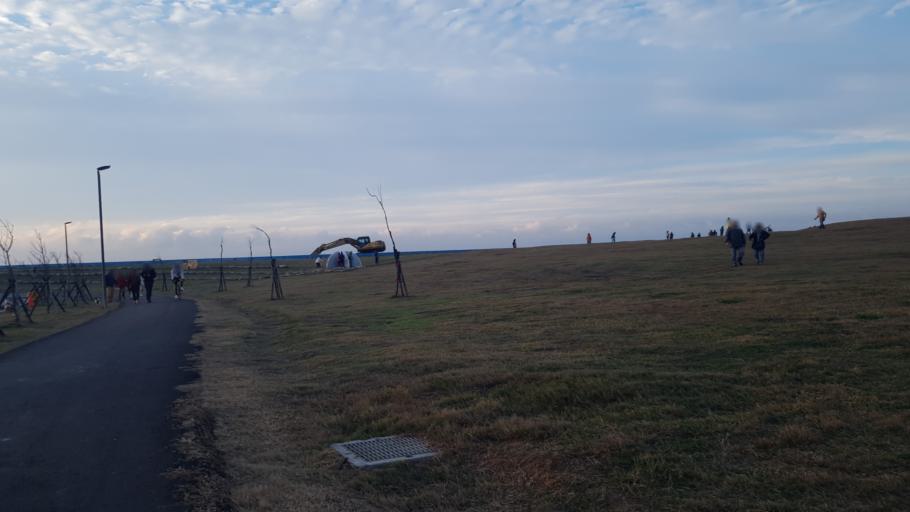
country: TW
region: Taiwan
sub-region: Hsinchu
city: Hsinchu
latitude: 24.8512
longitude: 120.9239
